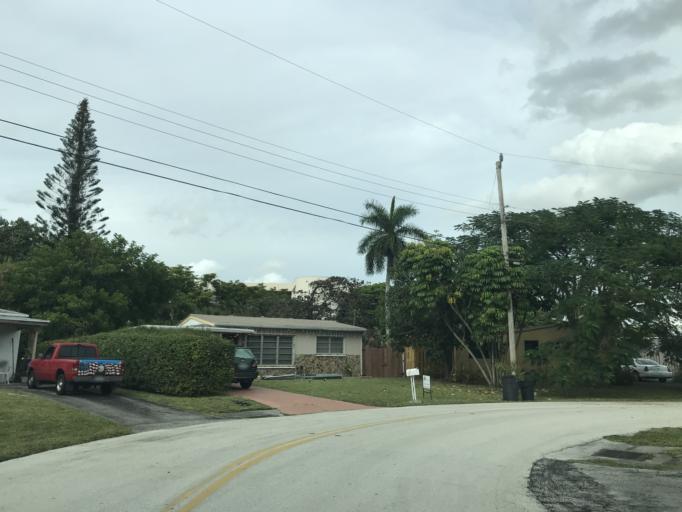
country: US
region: Florida
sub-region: Broward County
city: Margate
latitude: 26.2602
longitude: -80.2040
